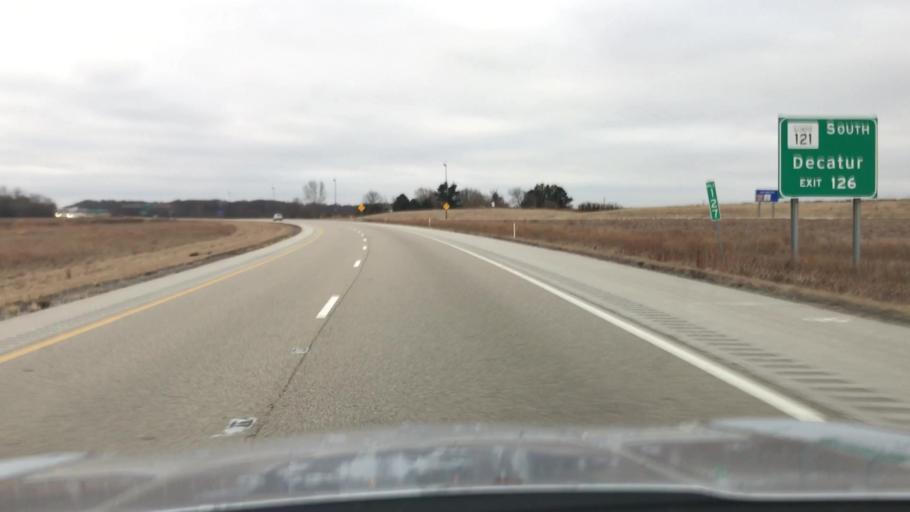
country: US
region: Illinois
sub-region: Logan County
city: Lincoln
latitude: 40.1774
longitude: -89.4169
